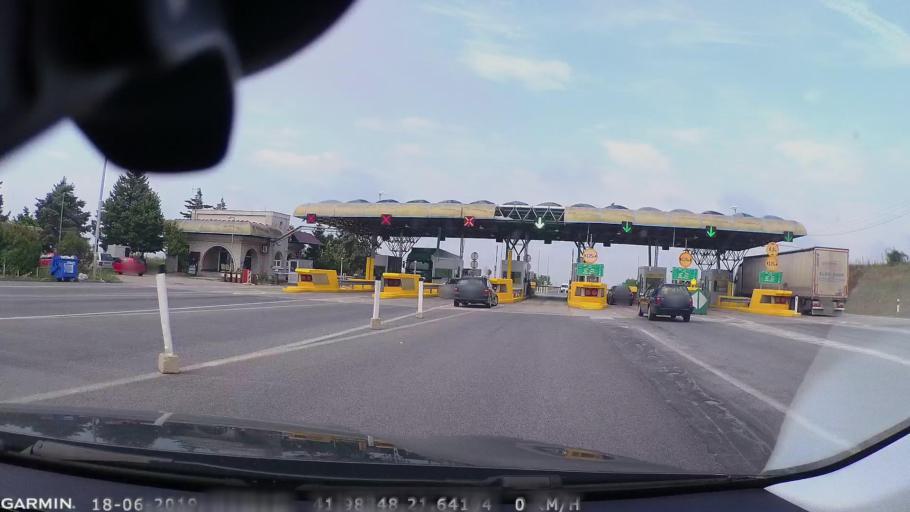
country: MK
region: Petrovec
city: Sredno Konjare
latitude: 41.9556
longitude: 21.7395
